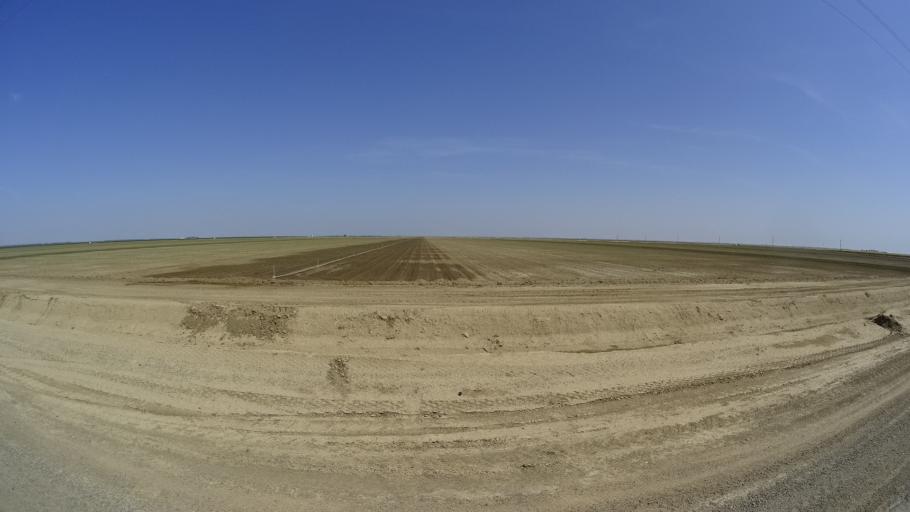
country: US
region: California
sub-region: Kings County
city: Kettleman City
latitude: 36.0942
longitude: -119.9542
